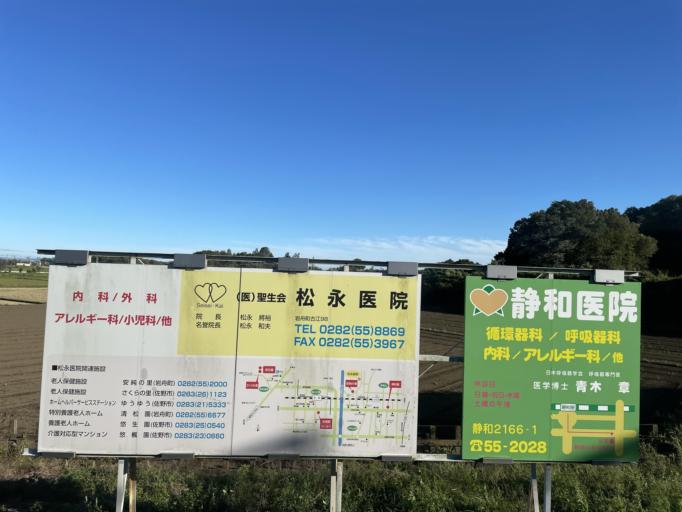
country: JP
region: Tochigi
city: Fujioka
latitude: 36.3167
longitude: 139.6852
